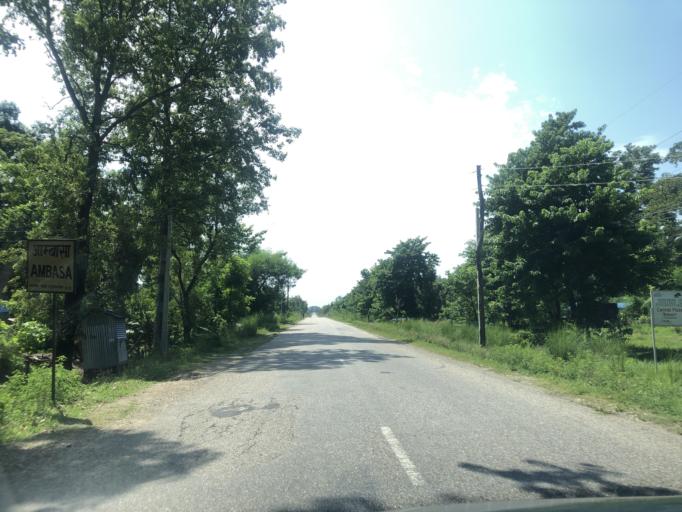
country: NP
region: Far Western
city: Tikapur
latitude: 28.5103
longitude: 81.3250
